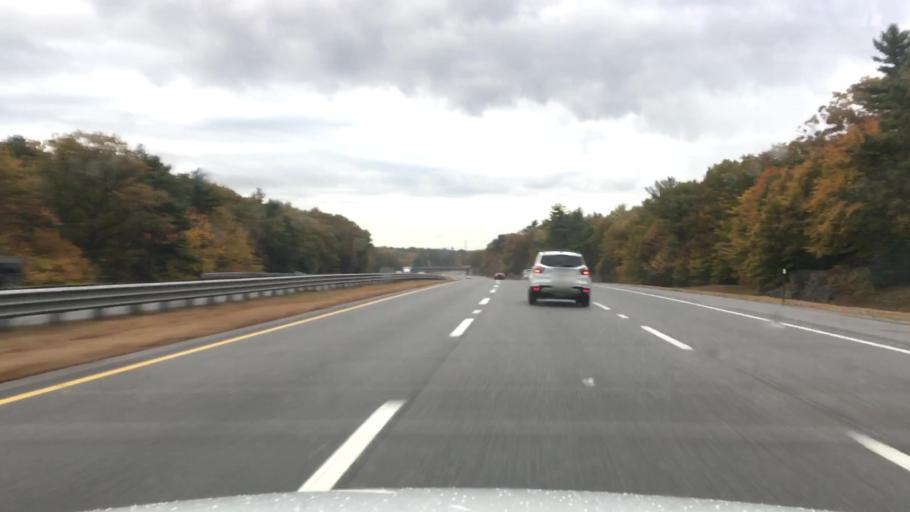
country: US
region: Maine
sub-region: York County
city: Cape Neddick
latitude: 43.2295
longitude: -70.6362
